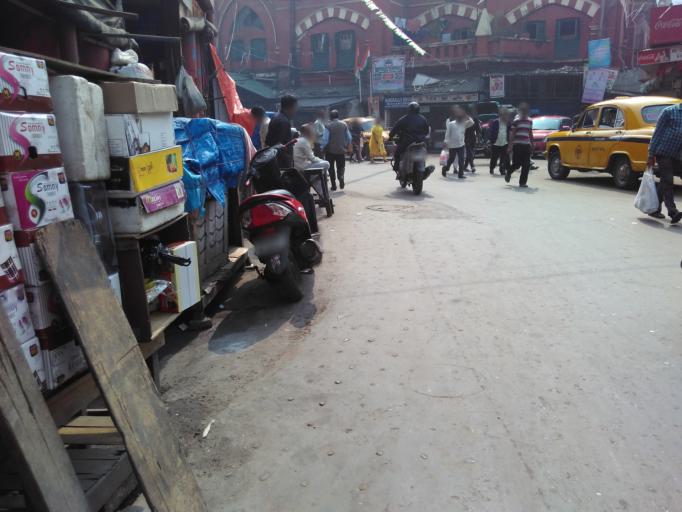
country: IN
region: West Bengal
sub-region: Kolkata
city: Bara Bazar
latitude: 22.5617
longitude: 88.3550
